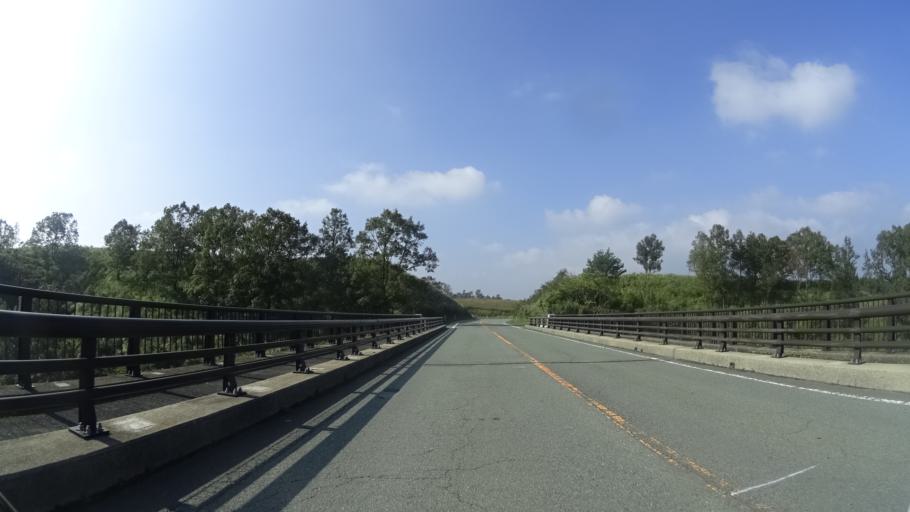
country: JP
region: Kumamoto
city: Aso
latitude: 33.0275
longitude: 131.0643
